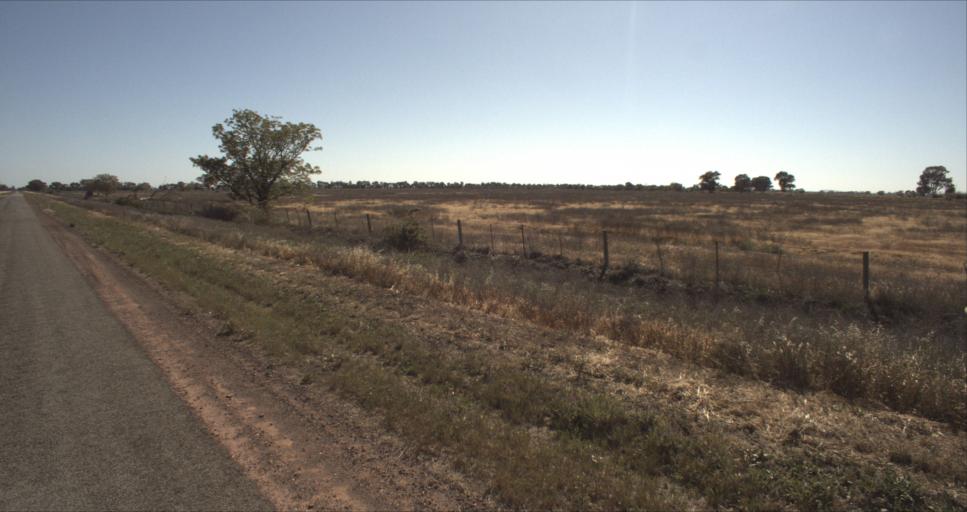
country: AU
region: New South Wales
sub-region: Leeton
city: Leeton
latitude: -34.5870
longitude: 146.2604
